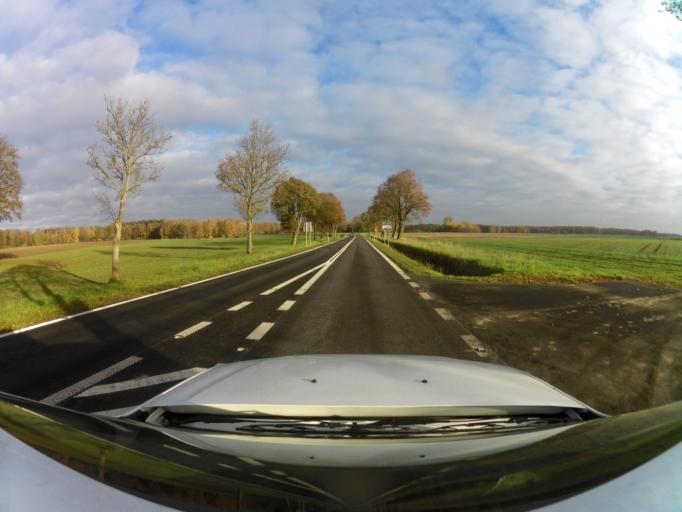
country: PL
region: West Pomeranian Voivodeship
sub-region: Powiat gryficki
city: Gryfice
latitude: 53.9813
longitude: 15.2383
